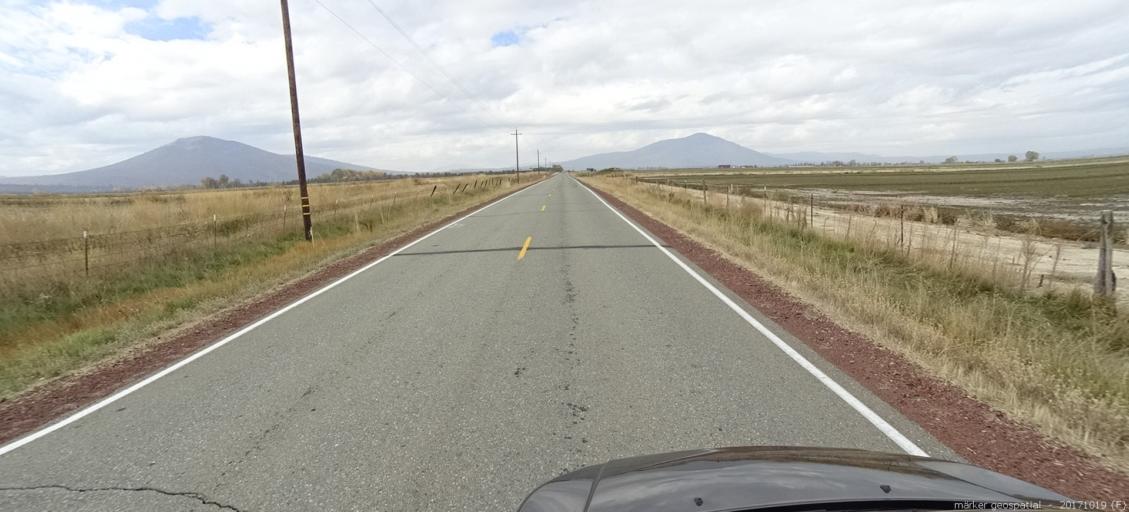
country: US
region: California
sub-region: Shasta County
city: Burney
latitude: 41.0508
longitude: -121.4357
